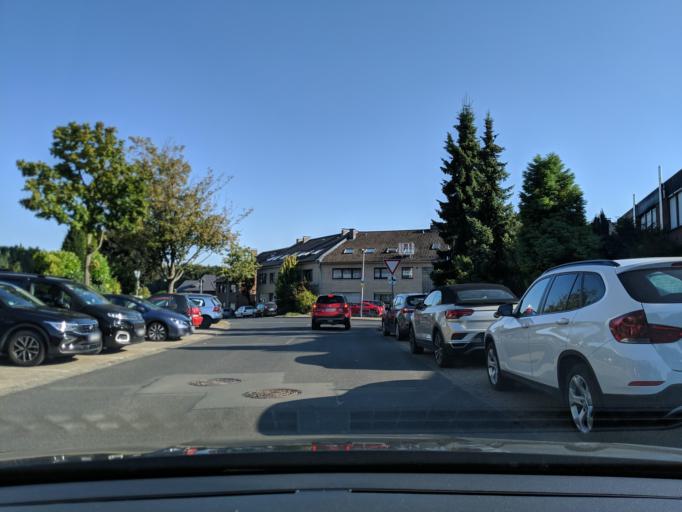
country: DE
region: North Rhine-Westphalia
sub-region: Regierungsbezirk Dusseldorf
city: Erkrath
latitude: 51.2035
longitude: 6.9262
